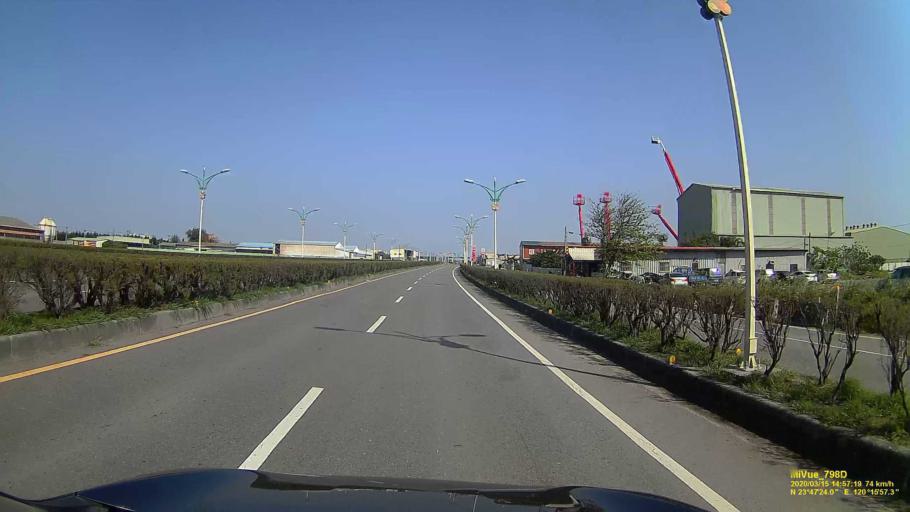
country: TW
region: Taiwan
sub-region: Yunlin
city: Douliu
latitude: 23.7900
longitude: 120.2663
